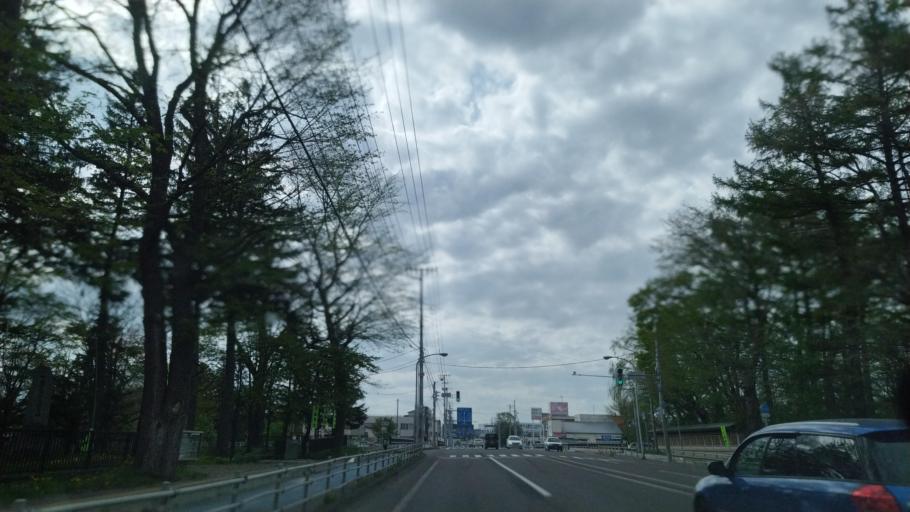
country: JP
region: Hokkaido
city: Obihiro
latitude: 42.9307
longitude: 143.2087
